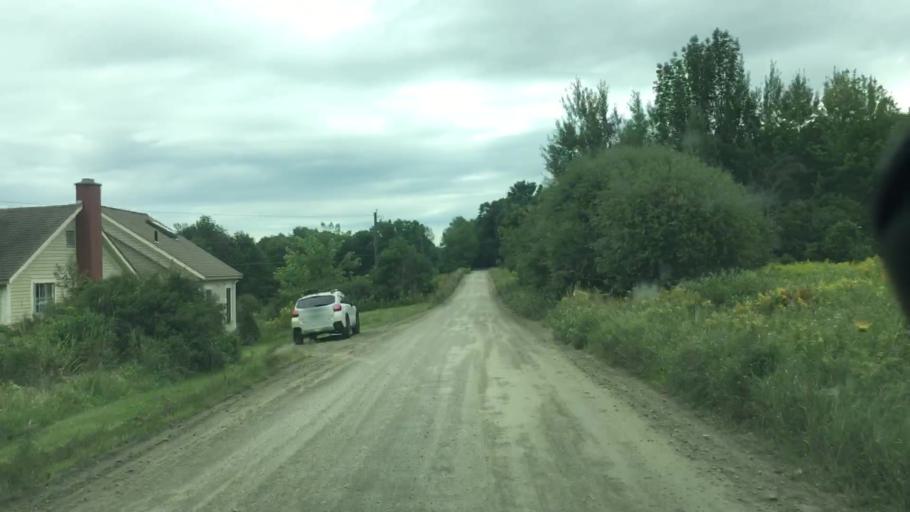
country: US
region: Vermont
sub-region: Windham County
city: Dover
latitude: 42.8572
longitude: -72.7804
